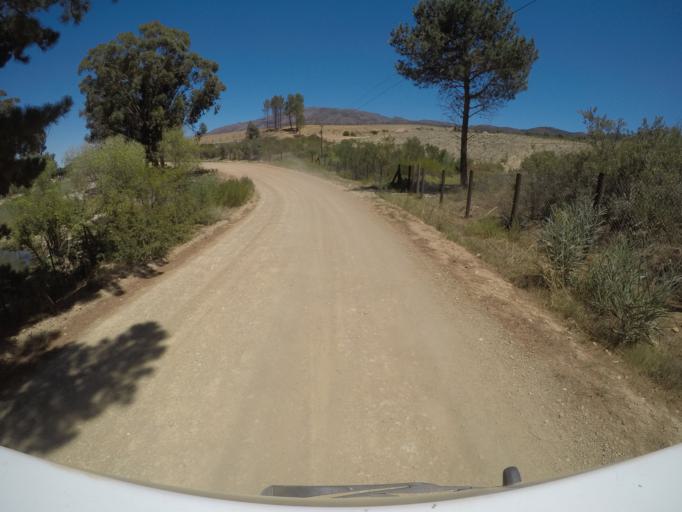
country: ZA
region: Western Cape
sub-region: Overberg District Municipality
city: Caledon
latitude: -34.1748
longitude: 19.2263
